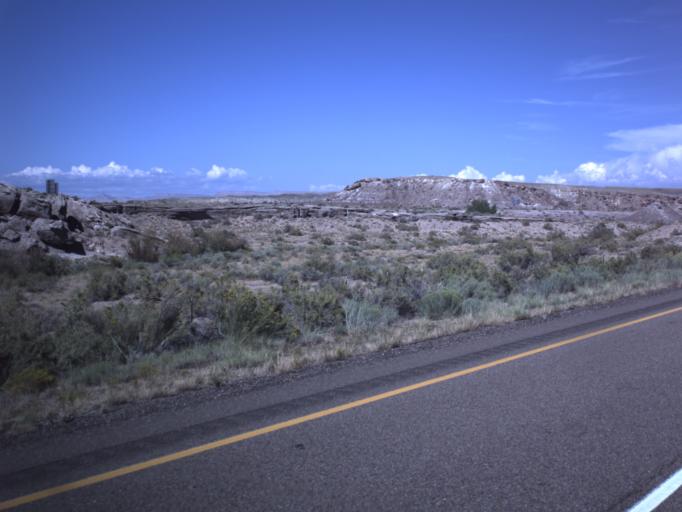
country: US
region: Utah
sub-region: Carbon County
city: East Carbon City
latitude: 38.9277
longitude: -110.3624
